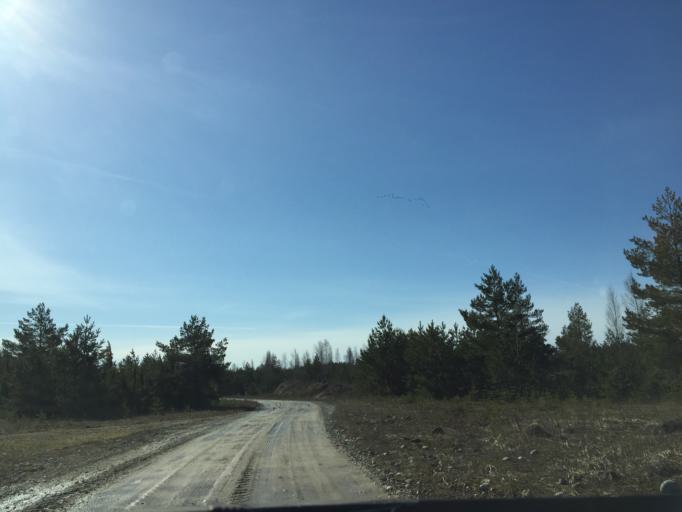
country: EE
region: Laeaene
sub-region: Haapsalu linn
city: Haapsalu
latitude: 58.6330
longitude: 23.5252
